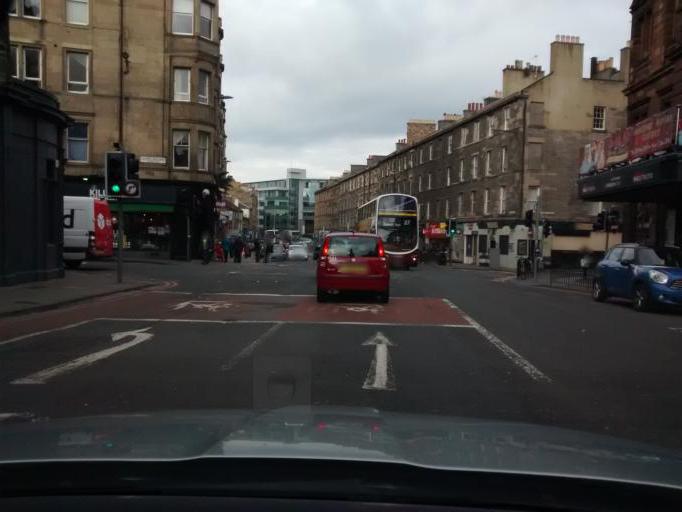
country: GB
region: Scotland
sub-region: Edinburgh
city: Edinburgh
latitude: 55.9417
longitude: -3.2035
